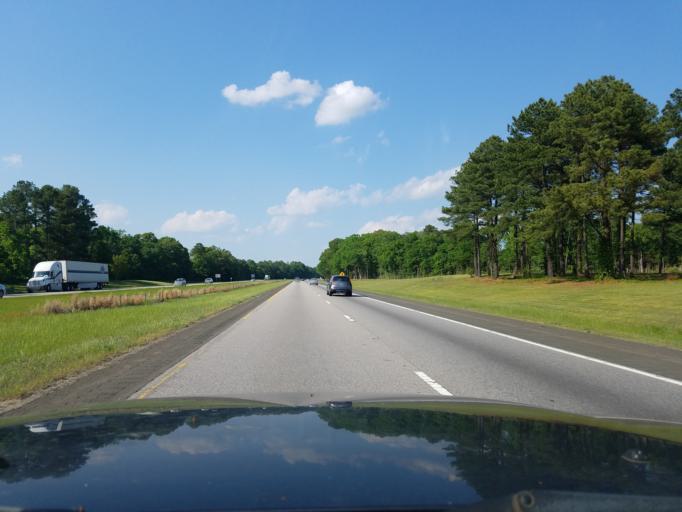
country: US
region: North Carolina
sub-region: Granville County
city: Butner
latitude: 36.1207
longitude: -78.7457
